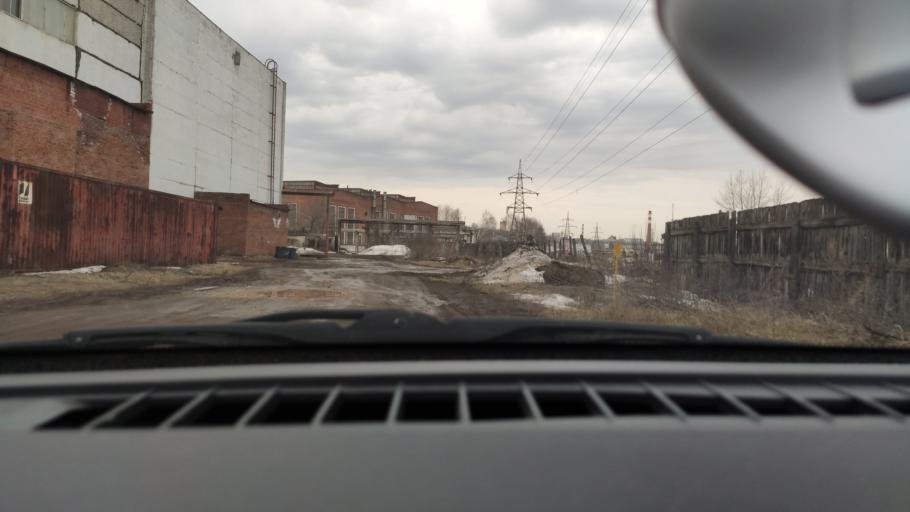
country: RU
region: Perm
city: Perm
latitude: 58.0415
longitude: 56.3071
